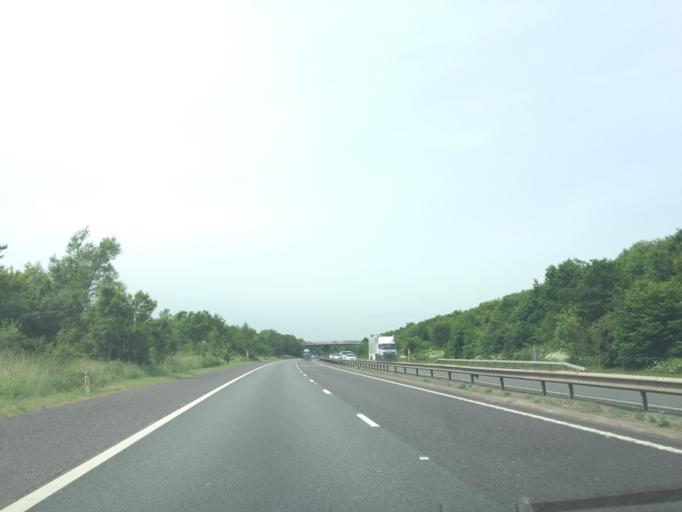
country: GB
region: England
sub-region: Kent
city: Borough Green
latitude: 51.3004
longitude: 0.3215
